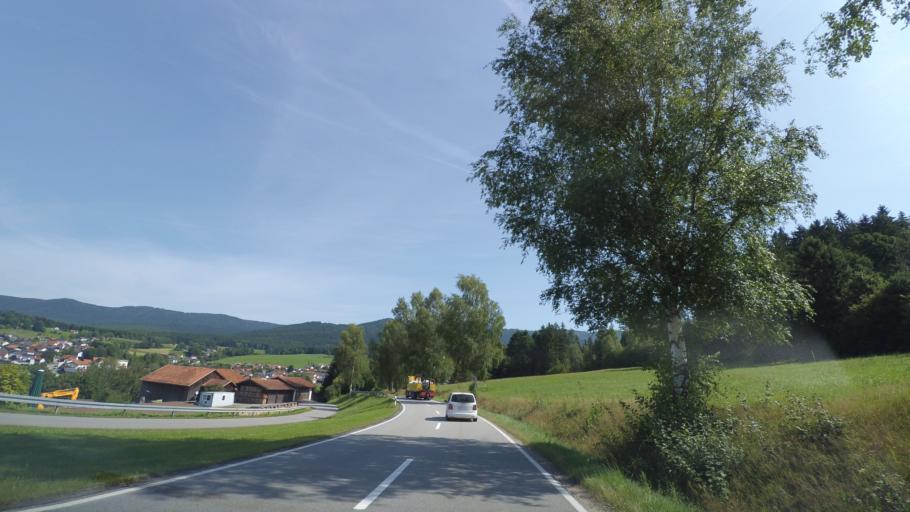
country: DE
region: Bavaria
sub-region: Lower Bavaria
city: Drachselsried
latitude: 49.0997
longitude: 13.0130
